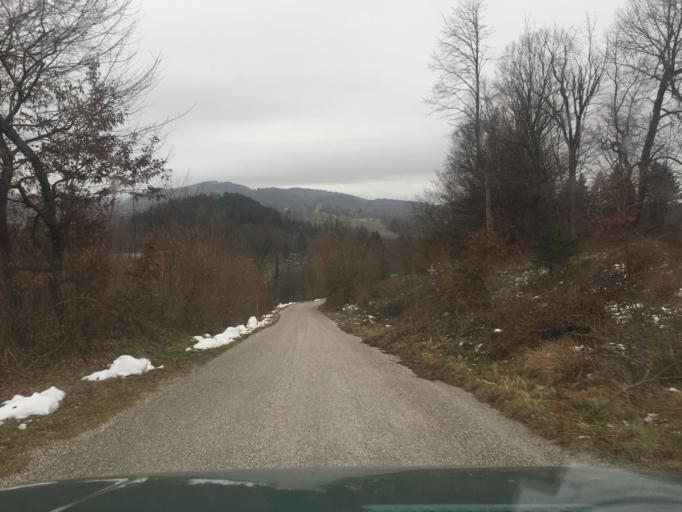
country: SI
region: Kanal
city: Kanal
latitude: 46.0693
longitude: 13.6960
